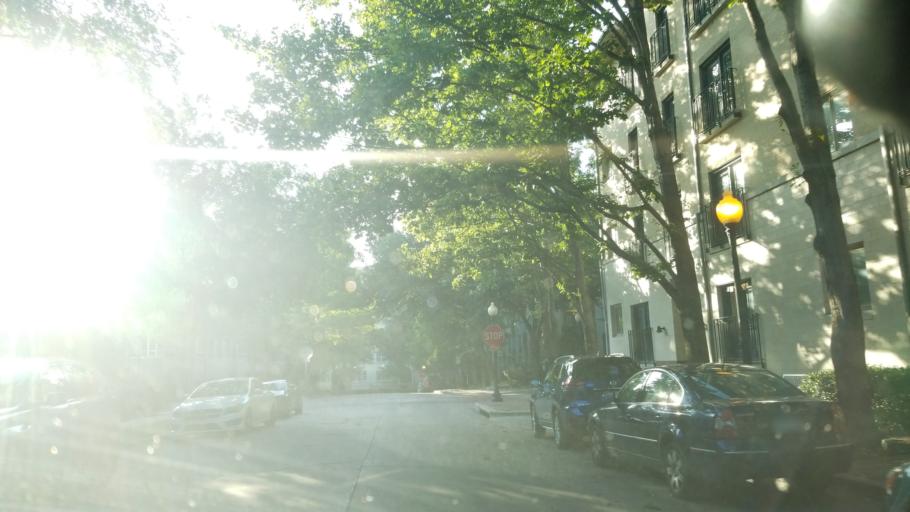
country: US
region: Texas
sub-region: Dallas County
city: Dallas
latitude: 32.8002
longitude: -96.8024
